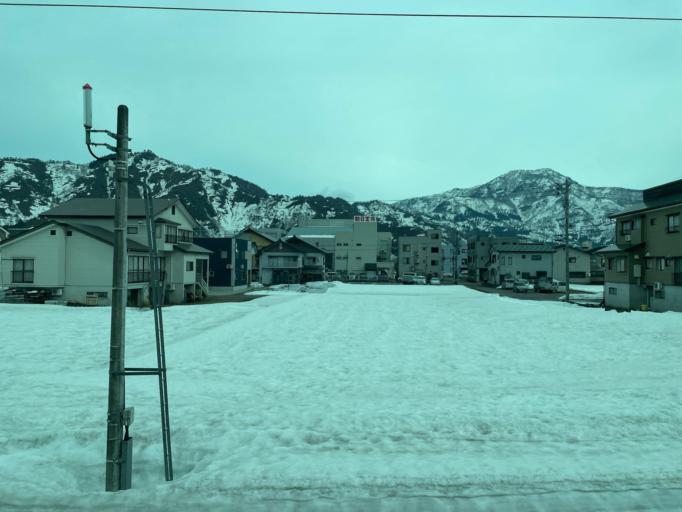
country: JP
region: Niigata
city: Muikamachi
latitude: 37.0616
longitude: 138.8725
